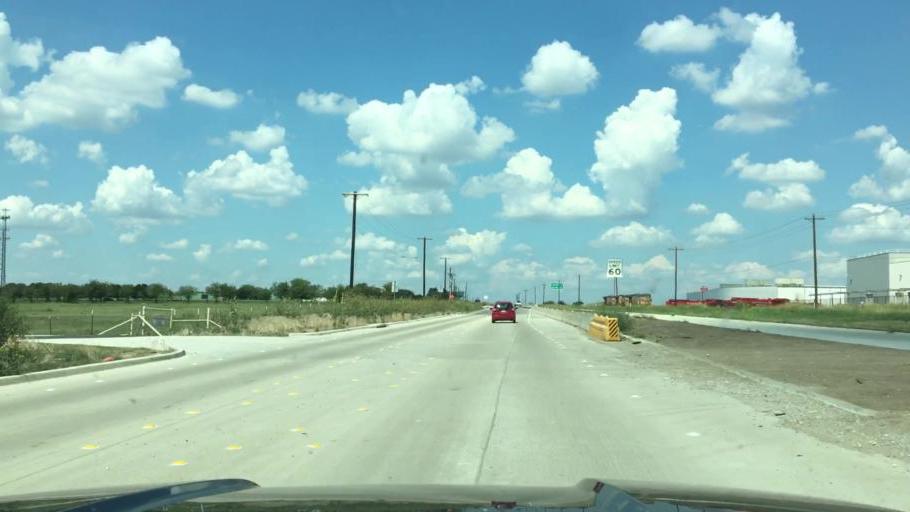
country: US
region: Texas
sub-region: Denton County
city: Justin
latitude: 33.0323
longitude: -97.3087
